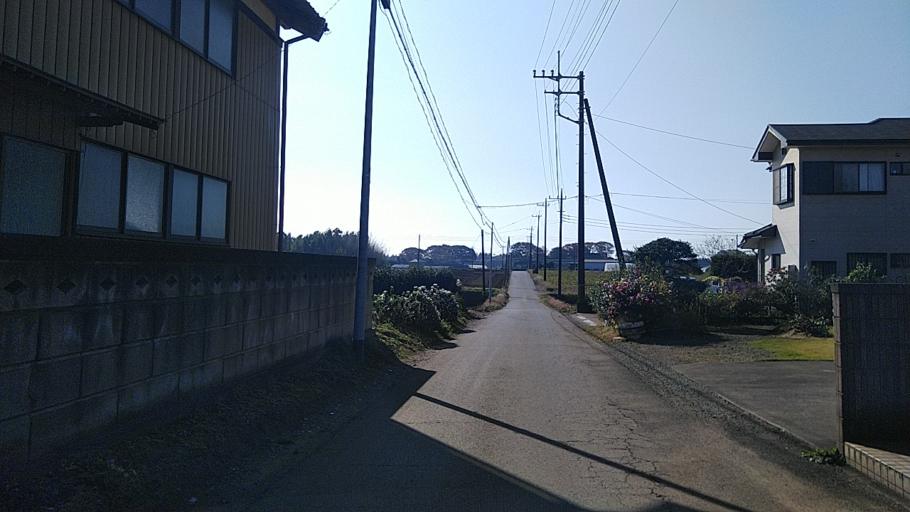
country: JP
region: Chiba
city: Sawara
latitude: 35.8405
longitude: 140.4684
